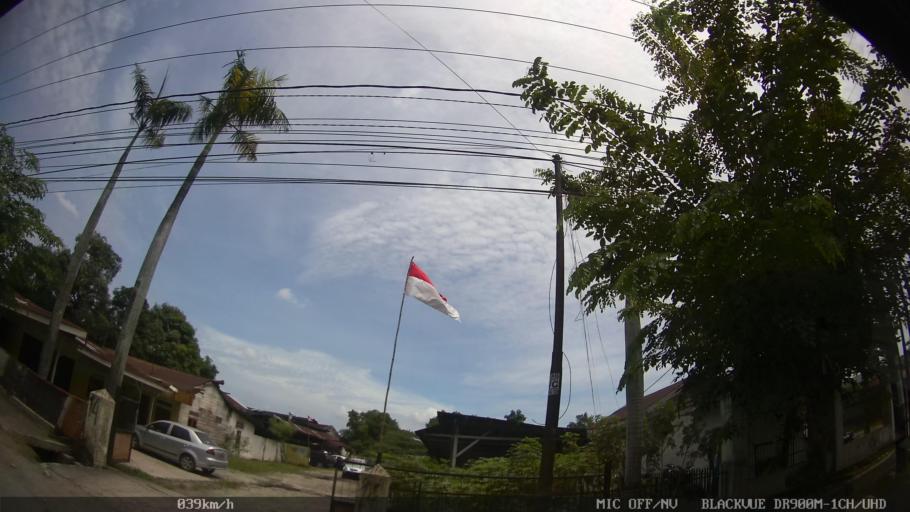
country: ID
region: North Sumatra
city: Sunggal
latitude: 3.5781
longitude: 98.6252
